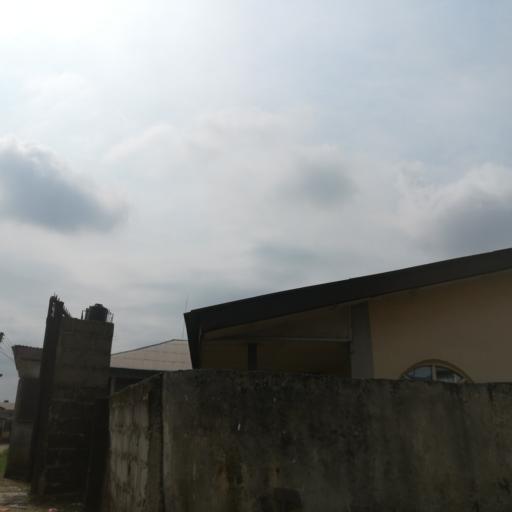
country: NG
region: Rivers
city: Port Harcourt
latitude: 4.8416
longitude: 7.0716
